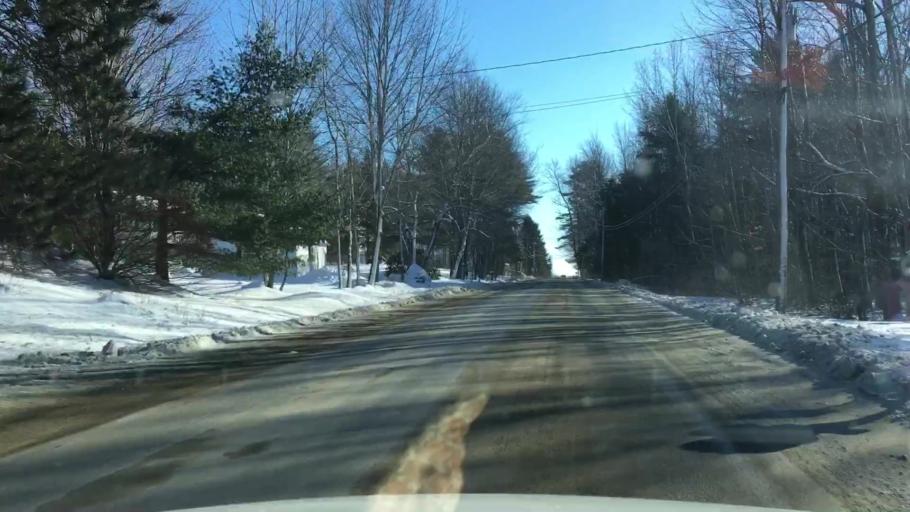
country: US
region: Maine
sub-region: Kennebec County
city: Winthrop
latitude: 44.3248
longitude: -69.9811
